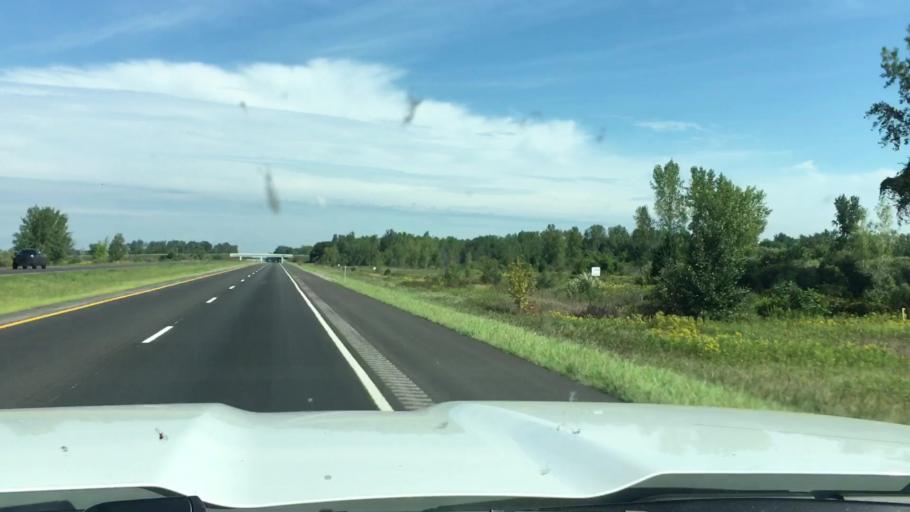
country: US
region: Michigan
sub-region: Saginaw County
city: Freeland
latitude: 43.5610
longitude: -84.1390
